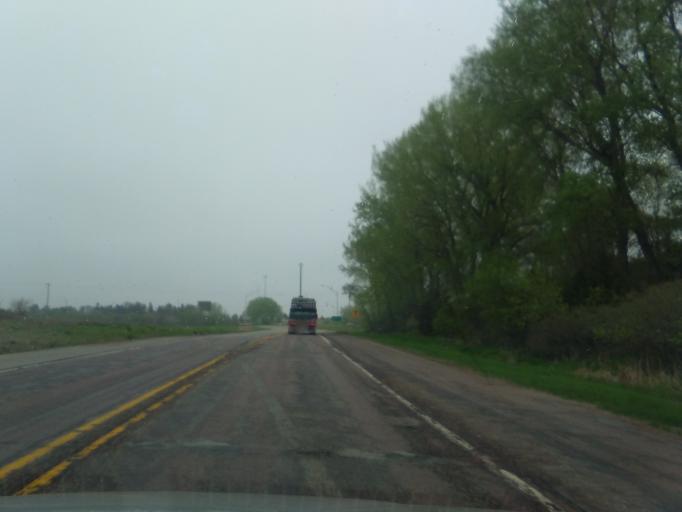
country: US
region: Nebraska
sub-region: Burt County
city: Oakland
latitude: 41.8225
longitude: -96.4682
